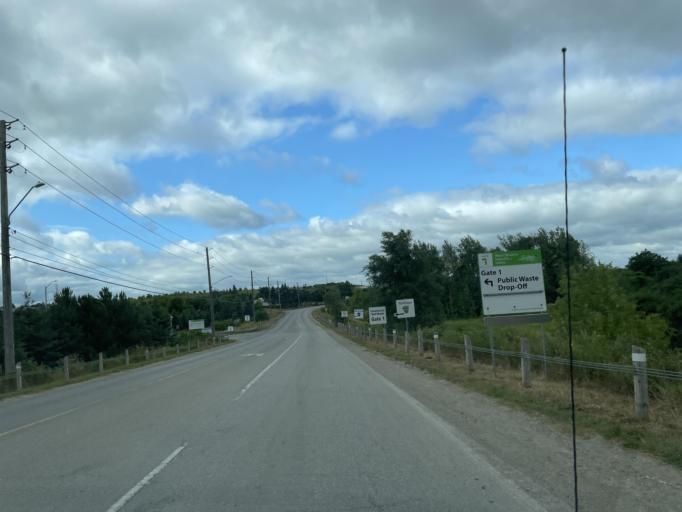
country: CA
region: Ontario
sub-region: Wellington County
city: Guelph
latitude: 43.5569
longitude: -80.1987
